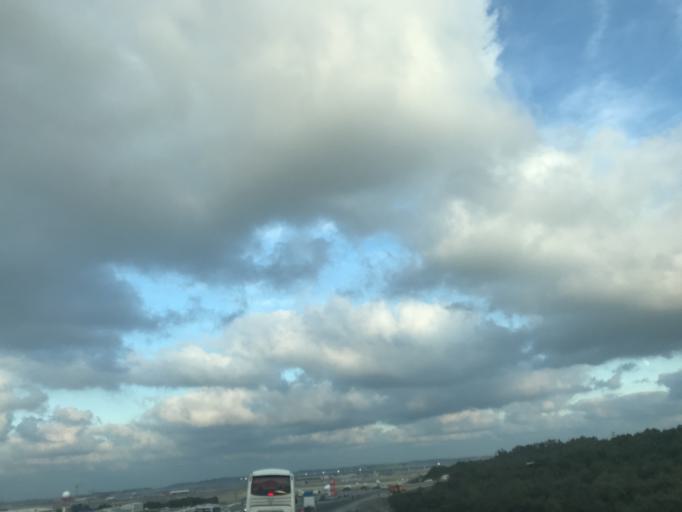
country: TR
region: Istanbul
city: Durusu
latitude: 41.2630
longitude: 28.6959
